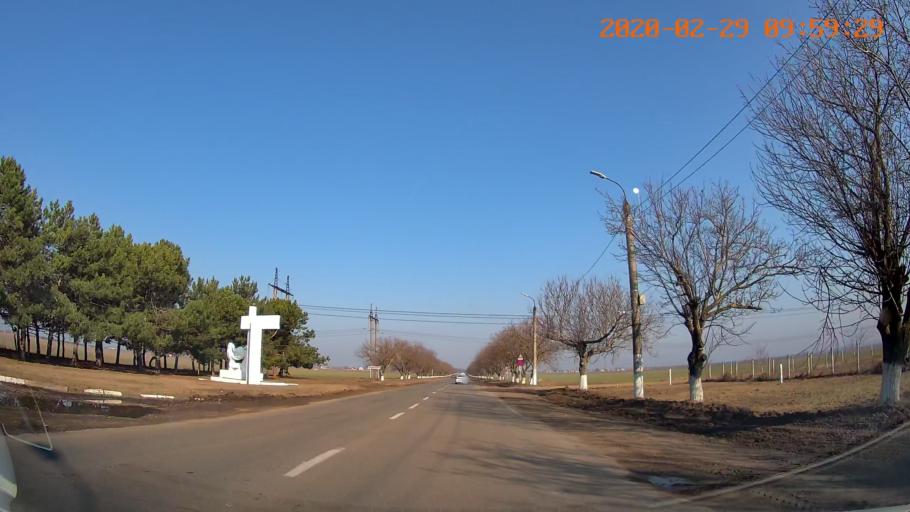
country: MD
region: Telenesti
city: Slobozia
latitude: 46.7574
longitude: 29.6883
